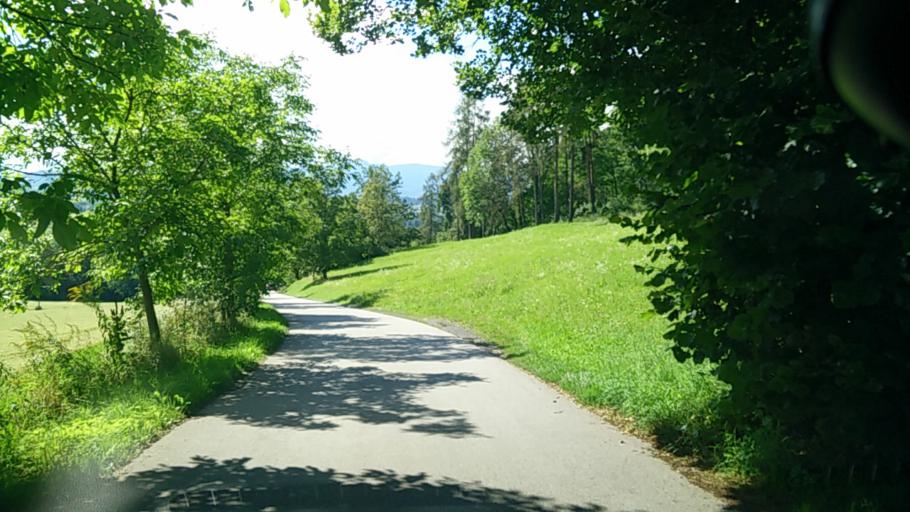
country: AT
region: Carinthia
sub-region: Politischer Bezirk Sankt Veit an der Glan
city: St. Georgen am Laengsee
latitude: 46.7536
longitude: 14.4530
